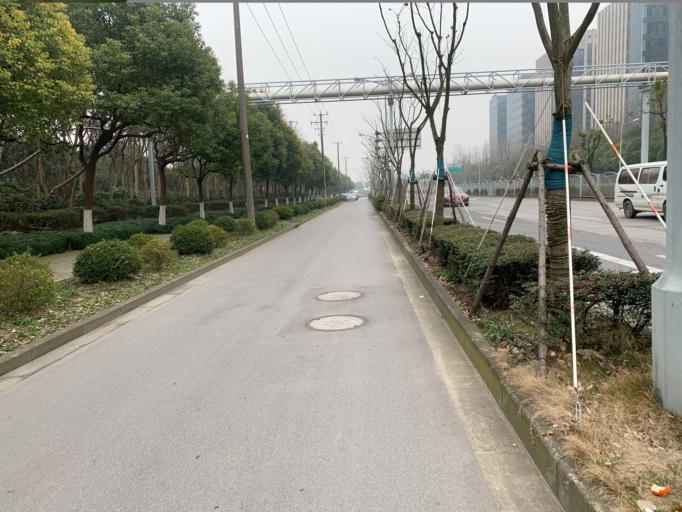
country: CN
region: Shanghai Shi
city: Huamu
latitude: 31.2478
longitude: 121.6212
